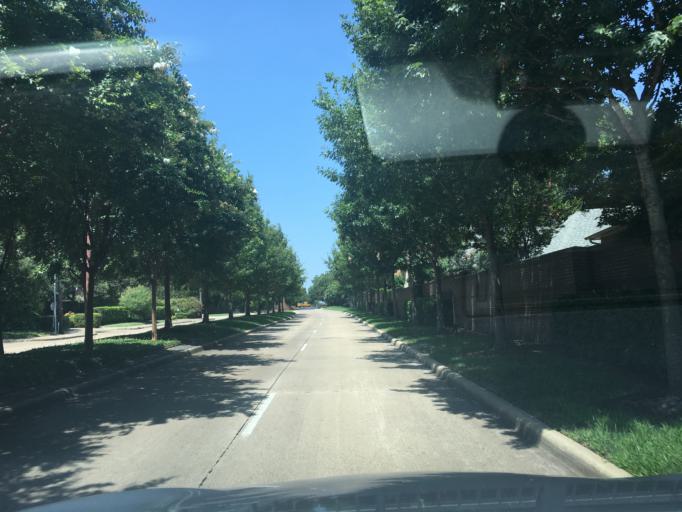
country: US
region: Texas
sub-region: Dallas County
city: Addison
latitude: 32.9172
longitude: -96.7892
